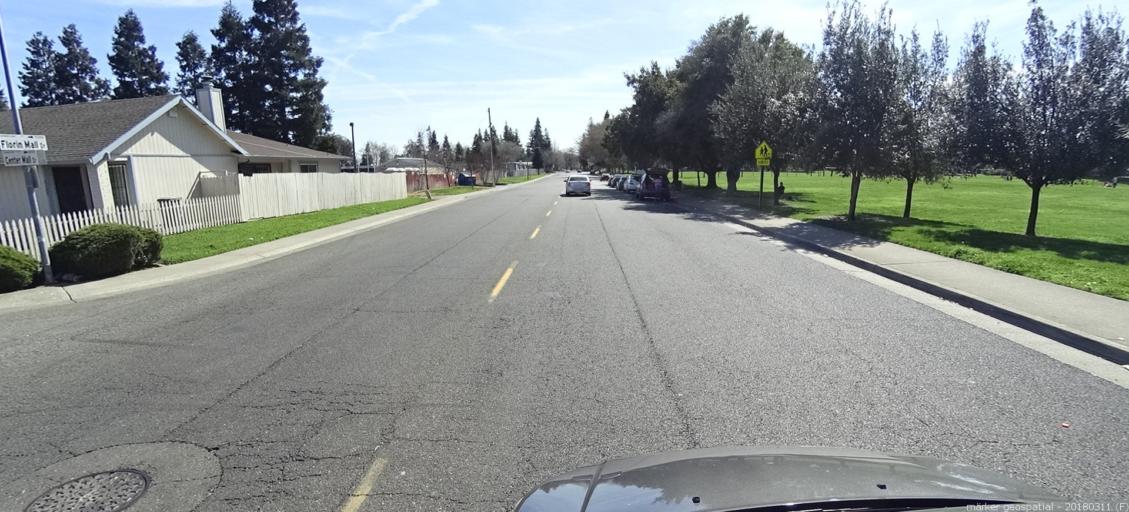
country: US
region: California
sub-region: Sacramento County
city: Parkway
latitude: 38.4912
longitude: -121.4342
